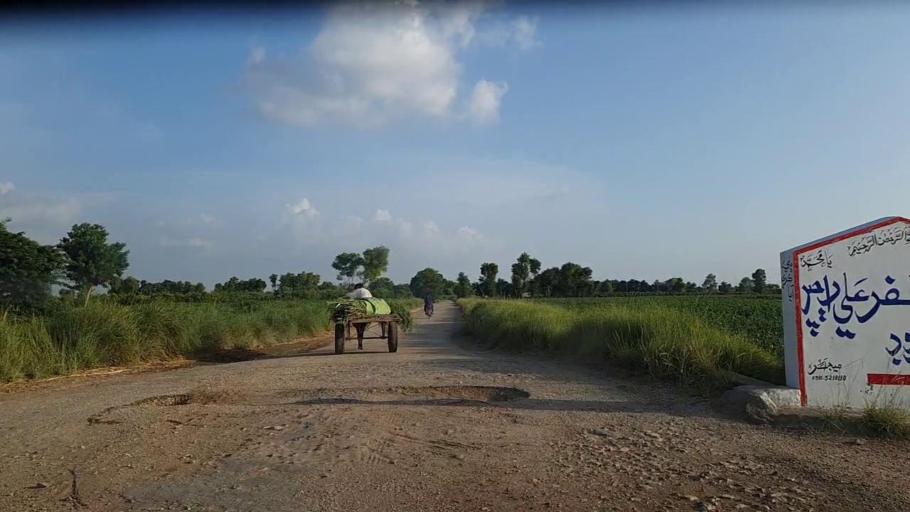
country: PK
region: Sindh
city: Hingorja
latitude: 27.0640
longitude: 68.4188
